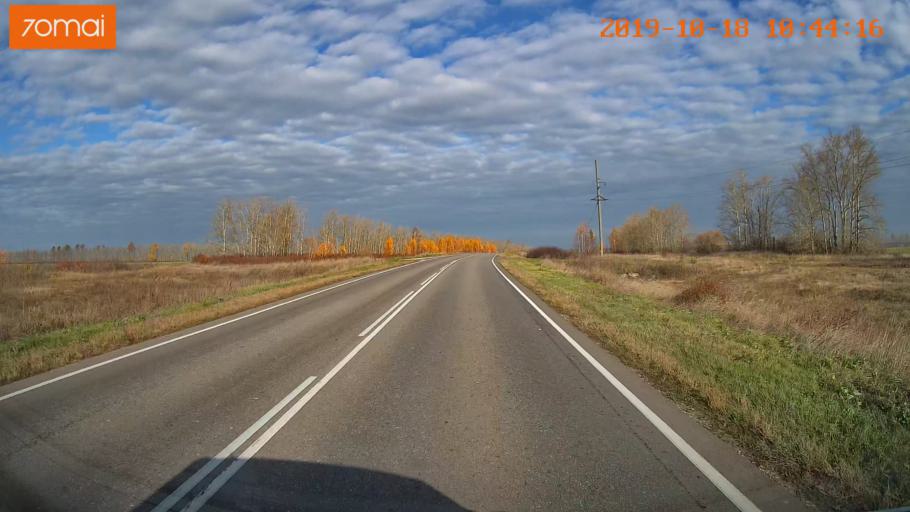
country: RU
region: Tula
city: Yepifan'
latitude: 53.6525
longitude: 38.6822
